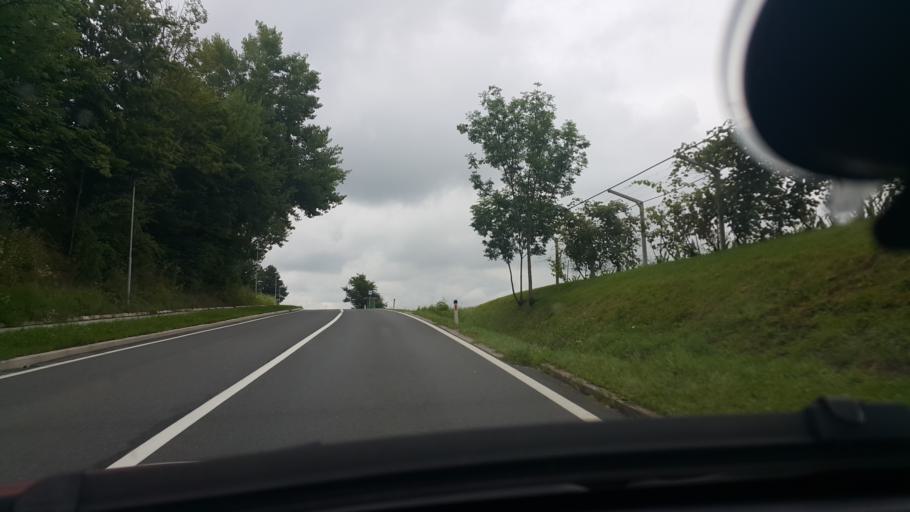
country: SI
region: Ormoz
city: Ormoz
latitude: 46.4103
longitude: 16.1216
